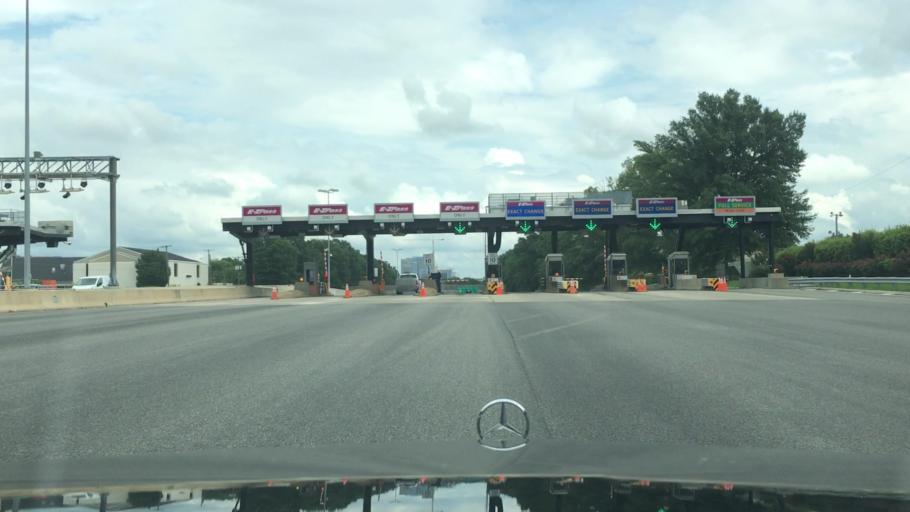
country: US
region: Virginia
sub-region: City of Richmond
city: Richmond
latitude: 37.5452
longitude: -77.4625
